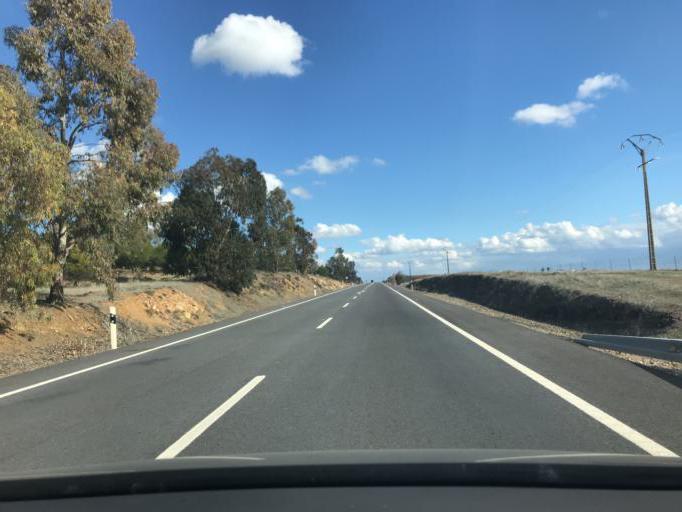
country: ES
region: Extremadura
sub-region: Provincia de Badajoz
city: Granja de Torrehermosa
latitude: 38.3006
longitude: -5.6002
